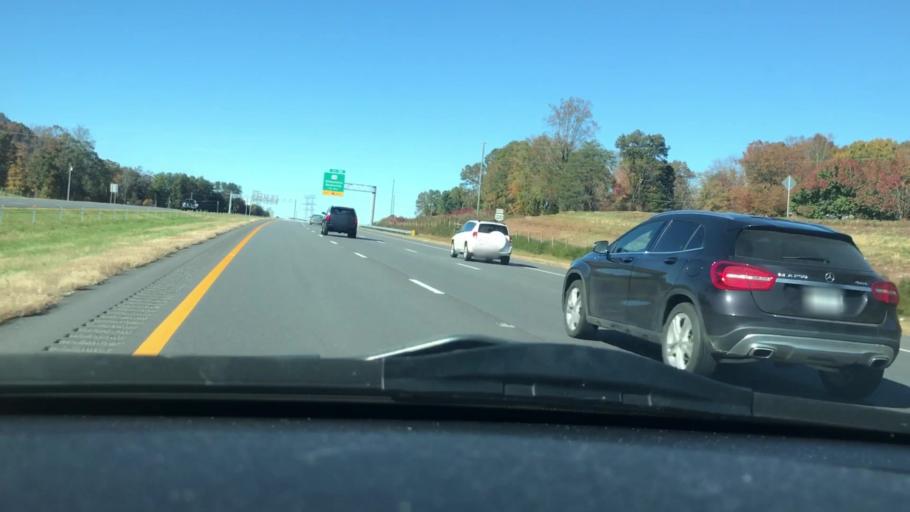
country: US
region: North Carolina
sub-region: Guilford County
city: Summerfield
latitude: 36.2349
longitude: -79.9172
